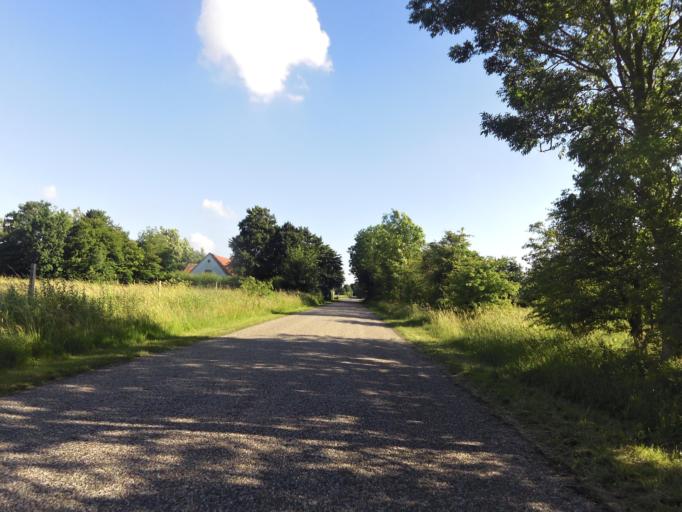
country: DK
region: South Denmark
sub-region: Vejen Kommune
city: Rodding
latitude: 55.3179
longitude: 9.1810
